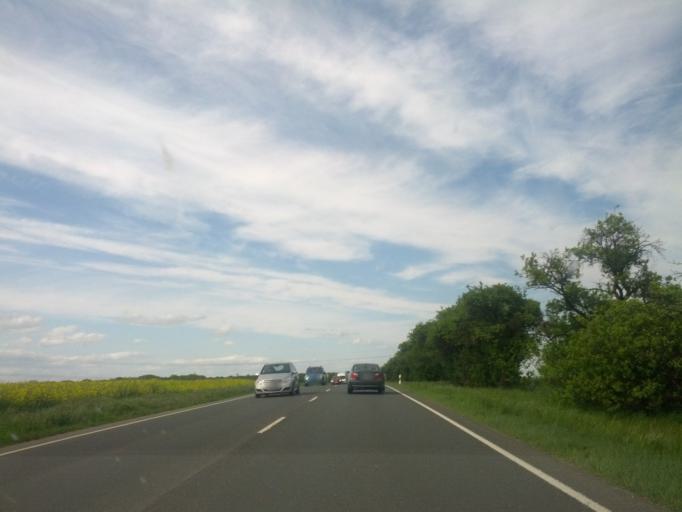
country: DE
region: Thuringia
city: Rockhausen
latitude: 50.9234
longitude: 11.0387
